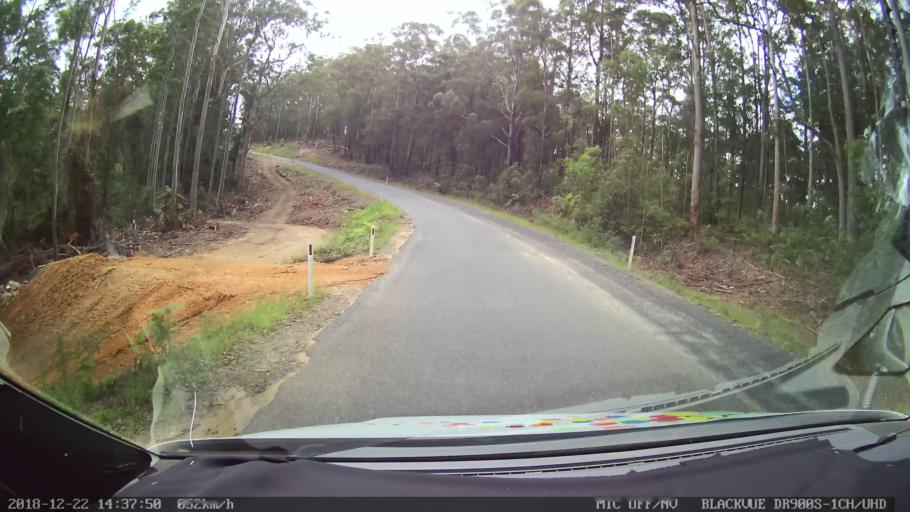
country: AU
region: New South Wales
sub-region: Bellingen
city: Dorrigo
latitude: -30.1345
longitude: 152.5999
